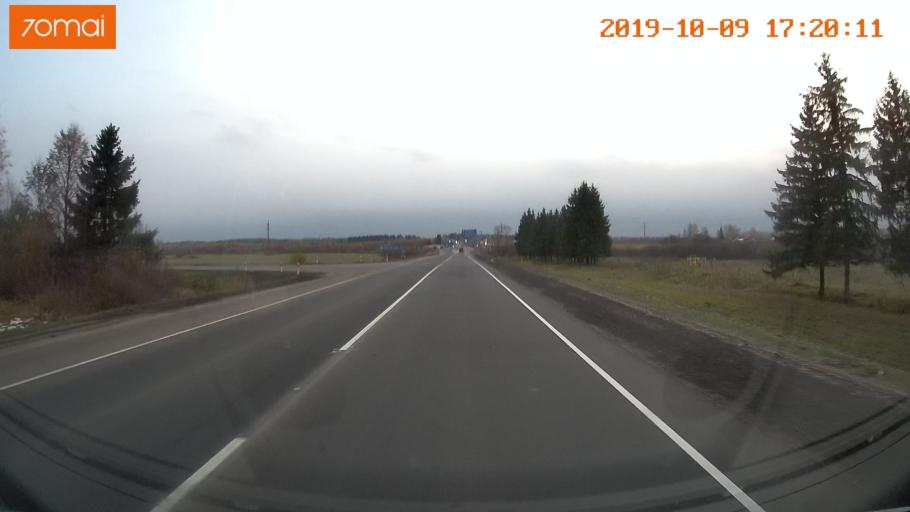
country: RU
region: Ivanovo
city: Furmanov
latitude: 57.2373
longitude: 41.1441
